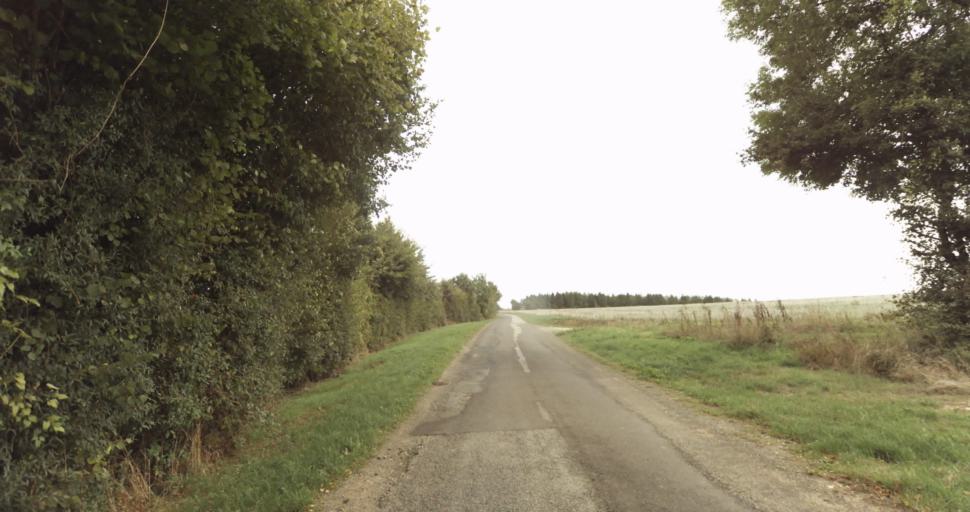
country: FR
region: Lower Normandy
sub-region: Departement de l'Orne
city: Sainte-Gauburge-Sainte-Colombe
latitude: 48.7412
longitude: 0.3664
